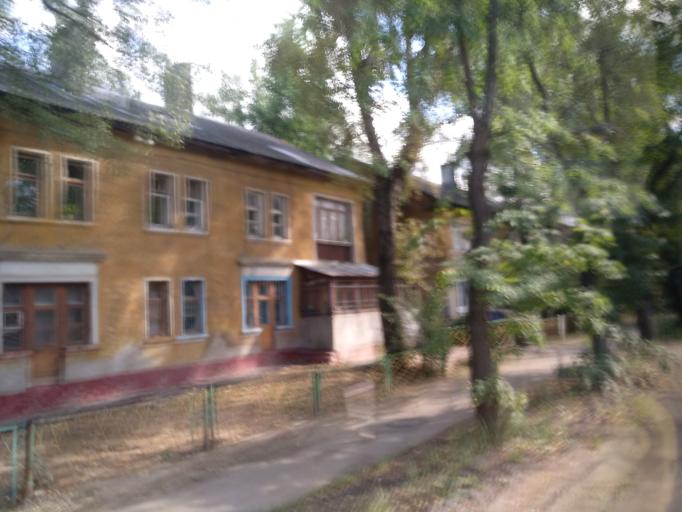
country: RU
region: Nizjnij Novgorod
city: Gorbatovka
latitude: 56.2462
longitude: 43.8288
